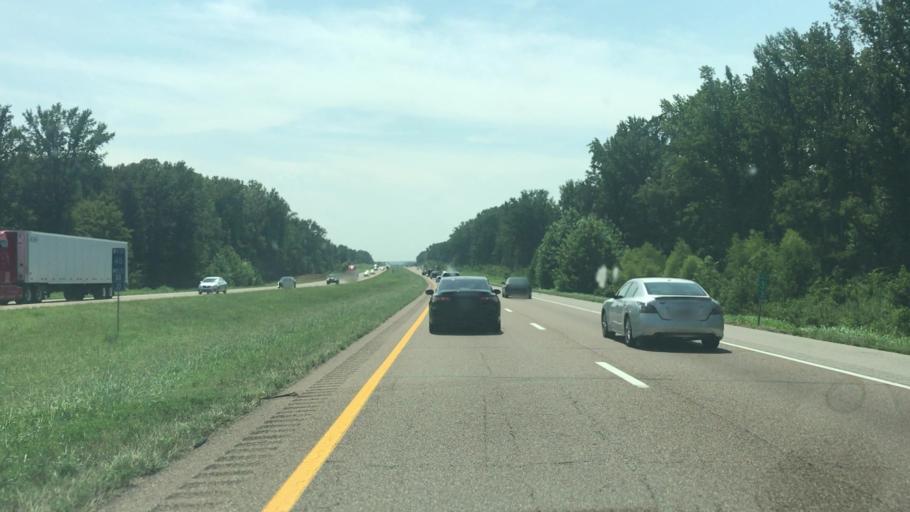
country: US
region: Tennessee
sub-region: Tipton County
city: Mason
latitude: 35.3313
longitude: -89.5556
